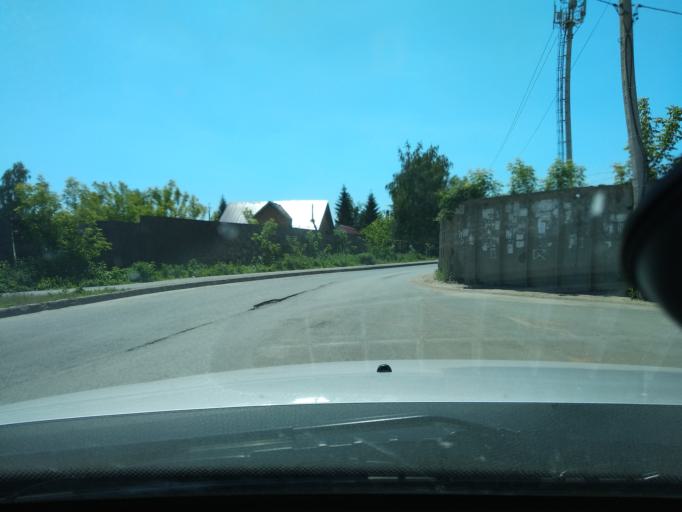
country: RU
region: Tatarstan
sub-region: Gorod Kazan'
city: Kazan
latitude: 55.8029
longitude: 49.2165
